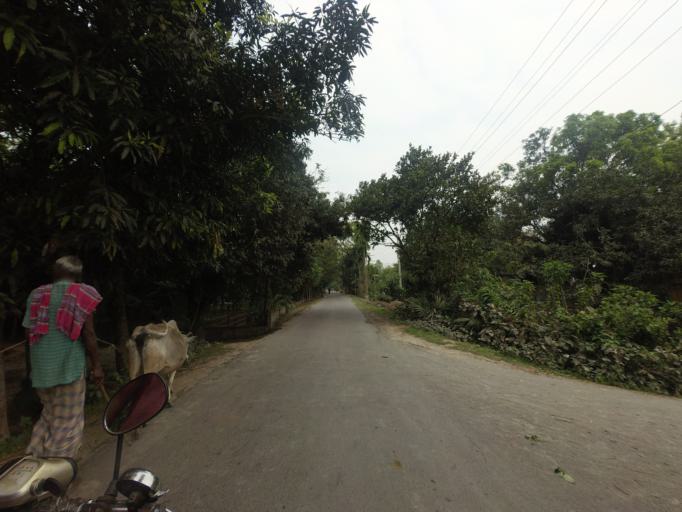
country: BD
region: Rajshahi
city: Sirajganj
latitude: 24.3671
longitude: 89.6715
